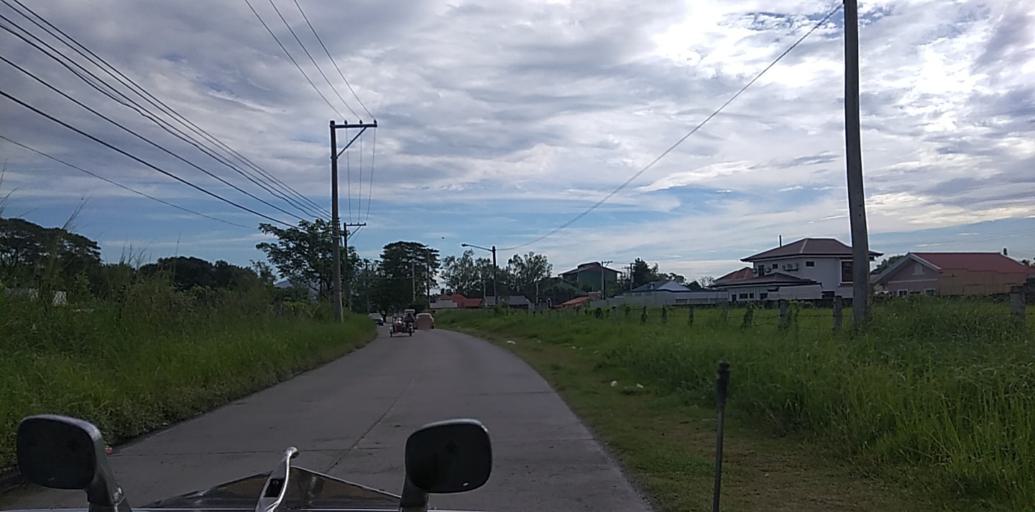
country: PH
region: Central Luzon
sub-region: Province of Pampanga
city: Telabastagan
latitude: 15.1067
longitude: 120.6096
